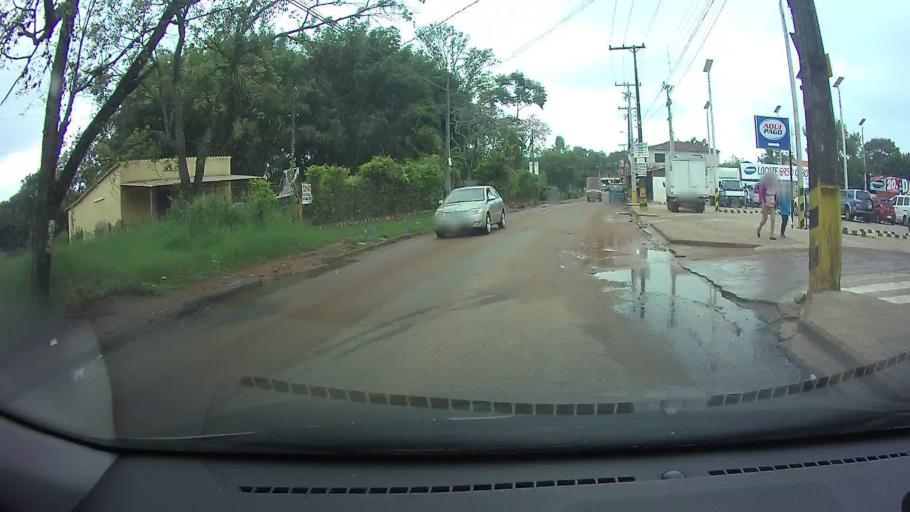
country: PY
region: Central
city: San Lorenzo
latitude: -25.3147
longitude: -57.4937
